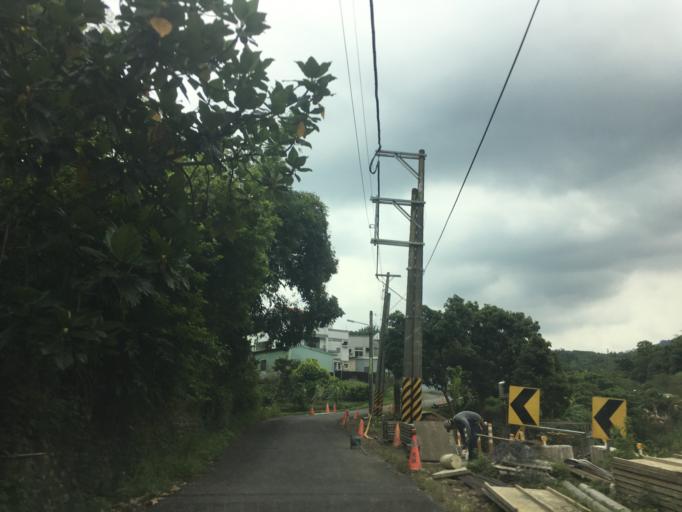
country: TW
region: Taiwan
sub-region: Taichung City
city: Taichung
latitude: 24.1667
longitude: 120.7563
